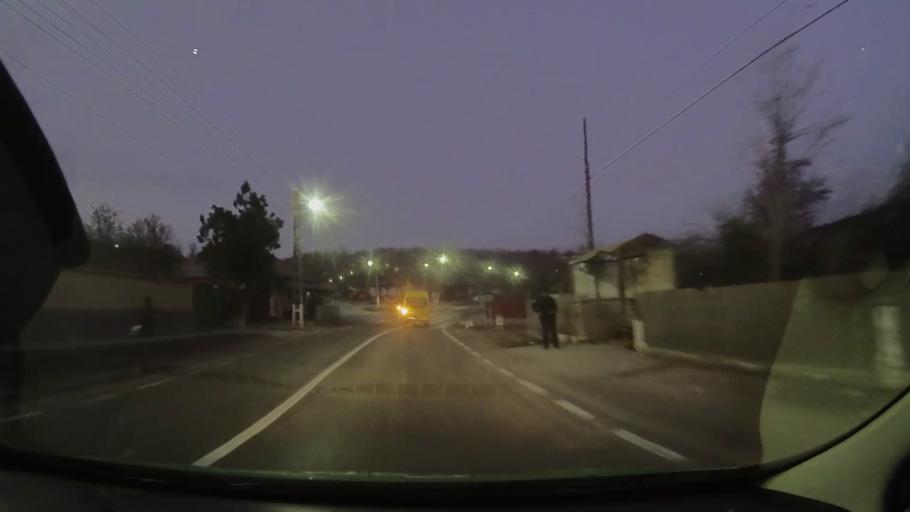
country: RO
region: Constanta
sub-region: Comuna Ion Corvin
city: Ion Corvin
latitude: 44.1136
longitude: 27.8066
